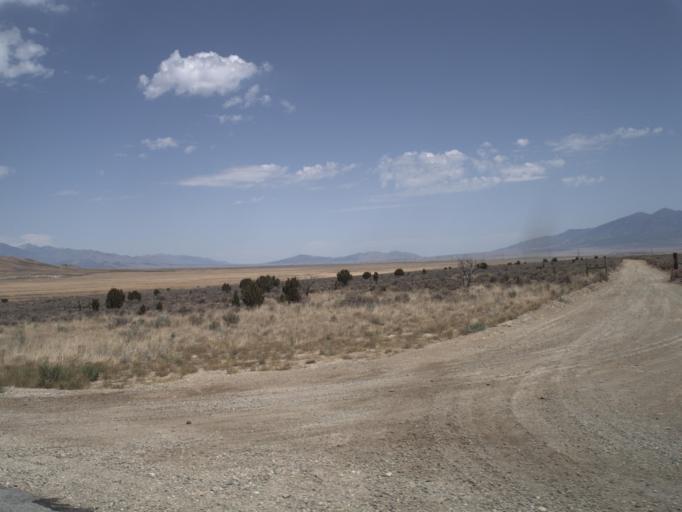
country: US
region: Utah
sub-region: Utah County
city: Eagle Mountain
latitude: 40.0684
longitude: -112.3274
